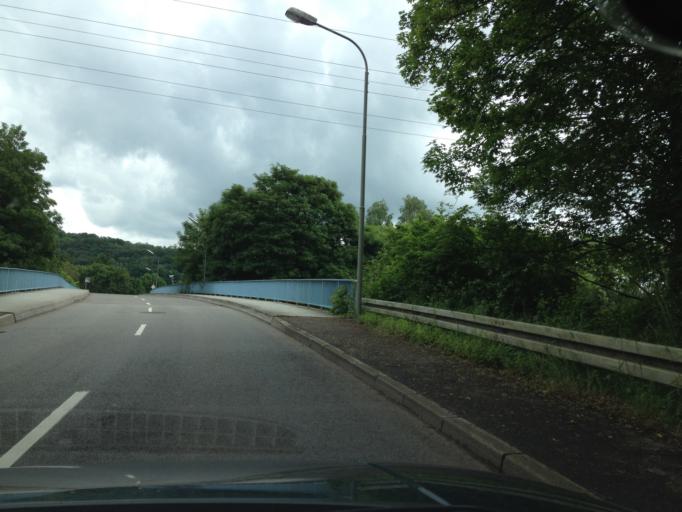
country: DE
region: Saarland
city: Homburg
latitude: 49.2837
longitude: 7.3125
